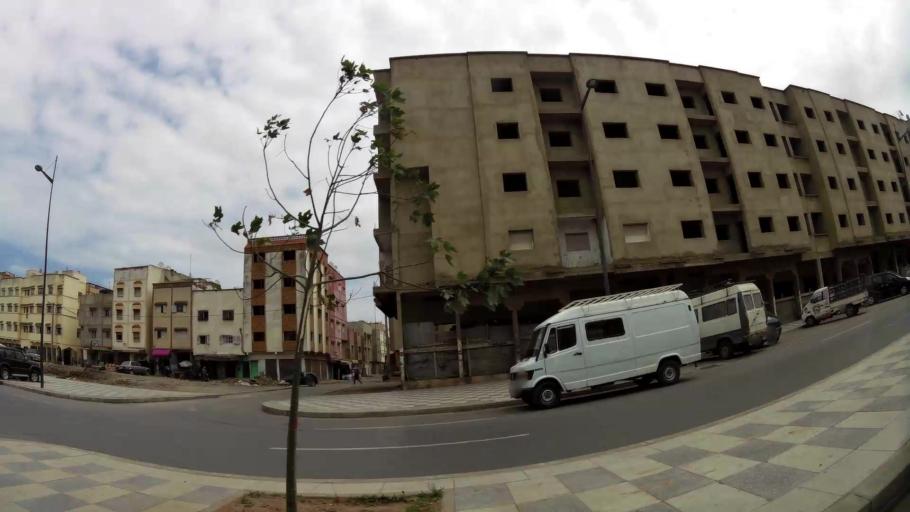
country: MA
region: Rabat-Sale-Zemmour-Zaer
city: Sale
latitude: 34.0599
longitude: -6.7807
